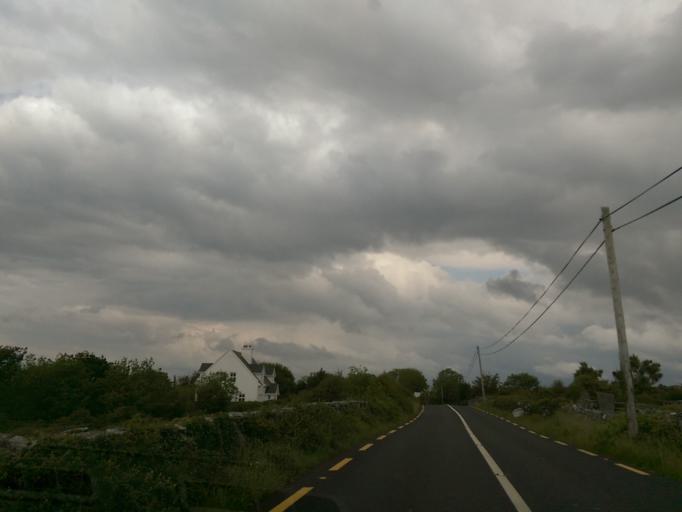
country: IE
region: Connaught
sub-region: County Galway
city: Bearna
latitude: 53.1322
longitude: -9.1164
